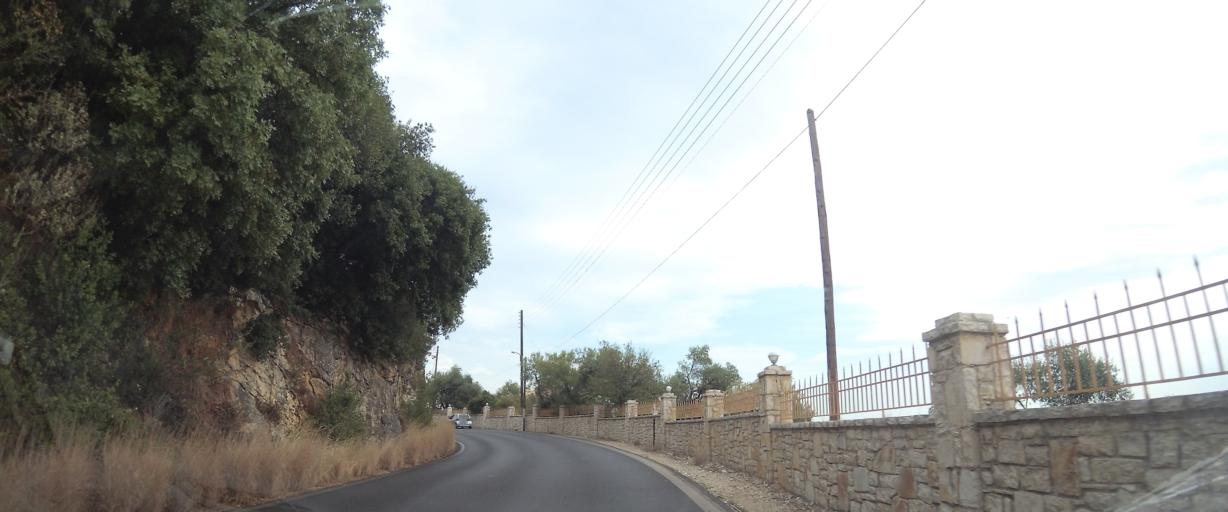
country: GR
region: Ionian Islands
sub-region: Nomos Kerkyras
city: Kontokali
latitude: 39.7241
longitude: 19.8911
